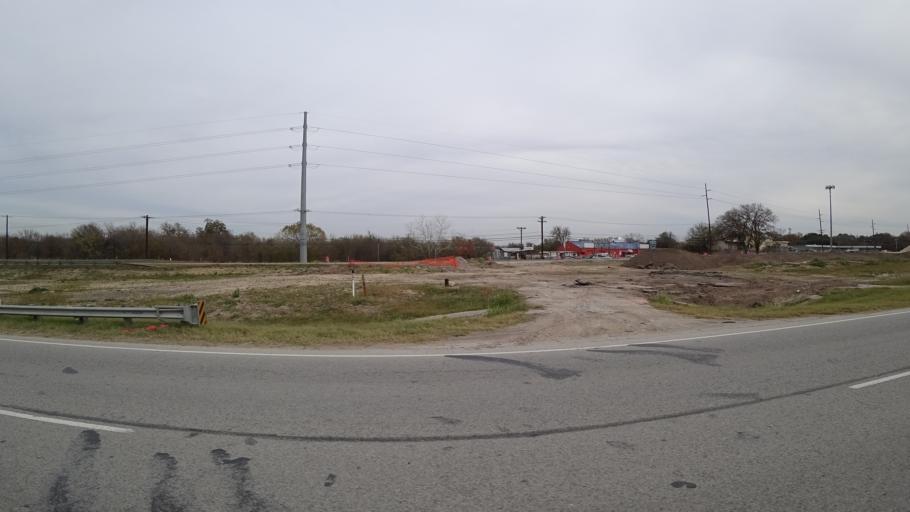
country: US
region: Texas
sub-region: Travis County
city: Austin
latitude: 30.2284
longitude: -97.6825
